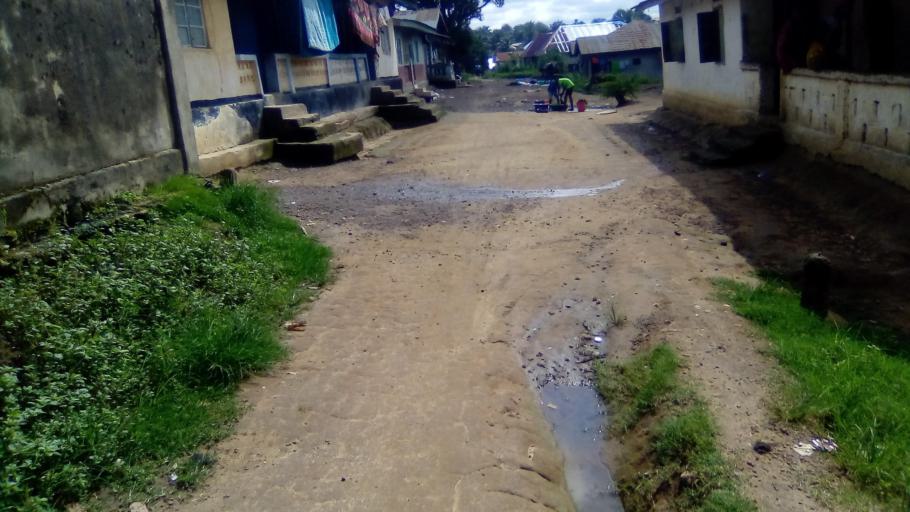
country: SL
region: Southern Province
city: Bo
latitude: 7.9765
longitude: -11.7254
